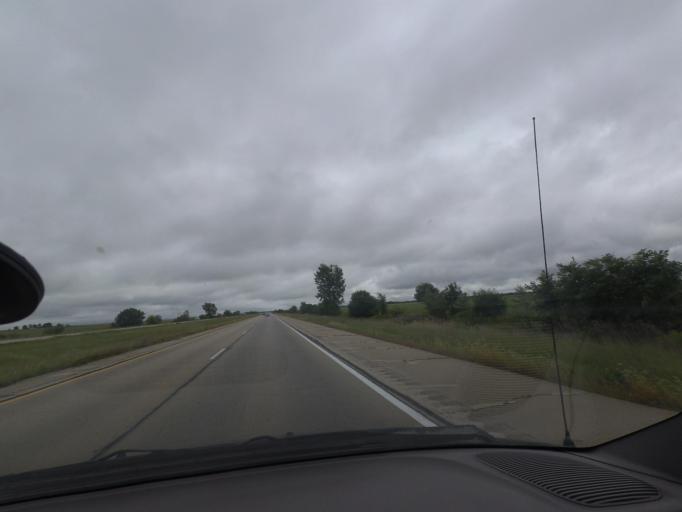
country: US
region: Illinois
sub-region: Piatt County
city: Cerro Gordo
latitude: 40.0206
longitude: -88.7061
